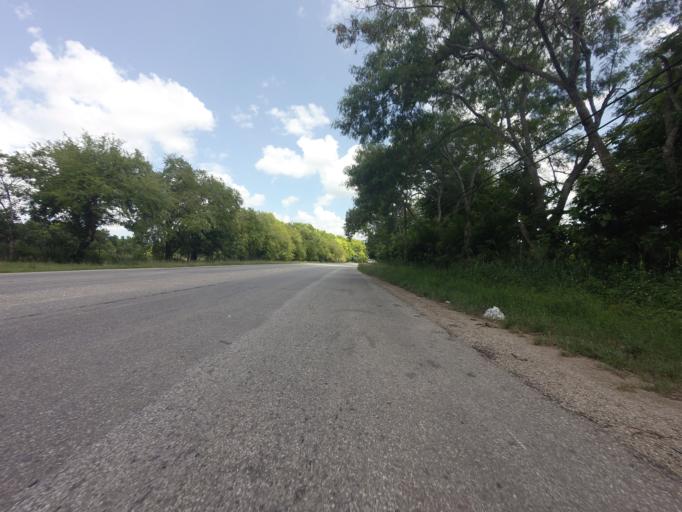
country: CU
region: La Habana
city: Arroyo Naranjo
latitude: 23.0376
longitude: -82.3410
